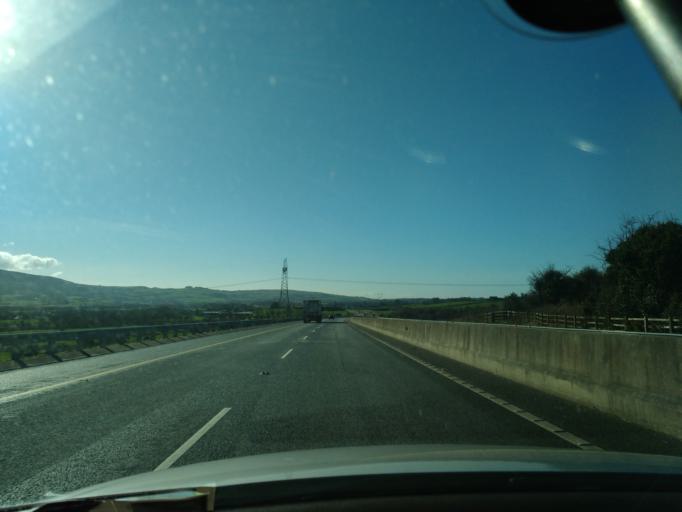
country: IE
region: Munster
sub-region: North Tipperary
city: Nenagh
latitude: 52.8318
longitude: -8.2918
